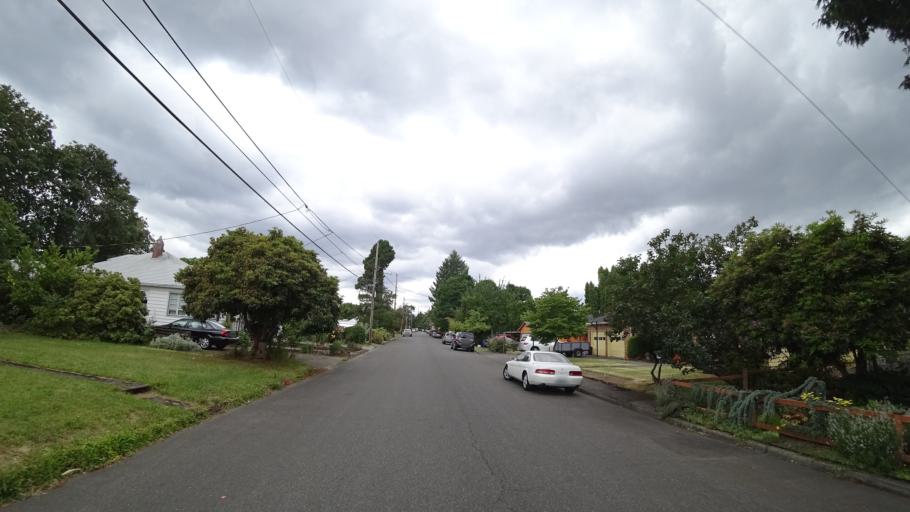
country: US
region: Oregon
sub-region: Multnomah County
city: Portland
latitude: 45.5615
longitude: -122.6165
